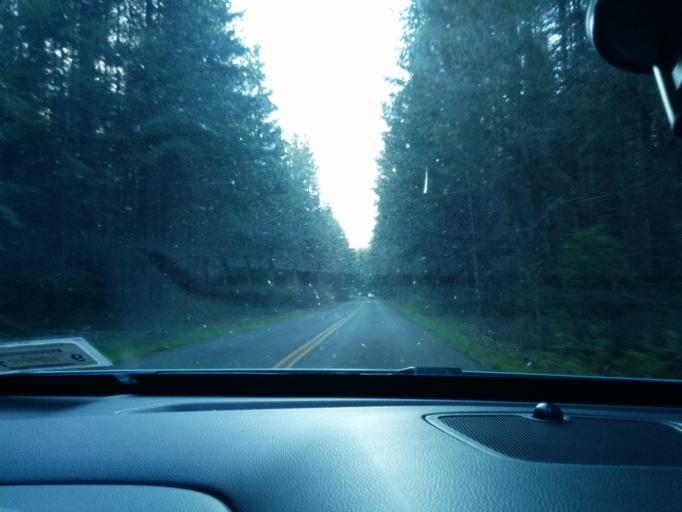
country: US
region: Washington
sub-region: Snohomish County
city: Gold Bar
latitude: 47.8957
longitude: -121.7431
